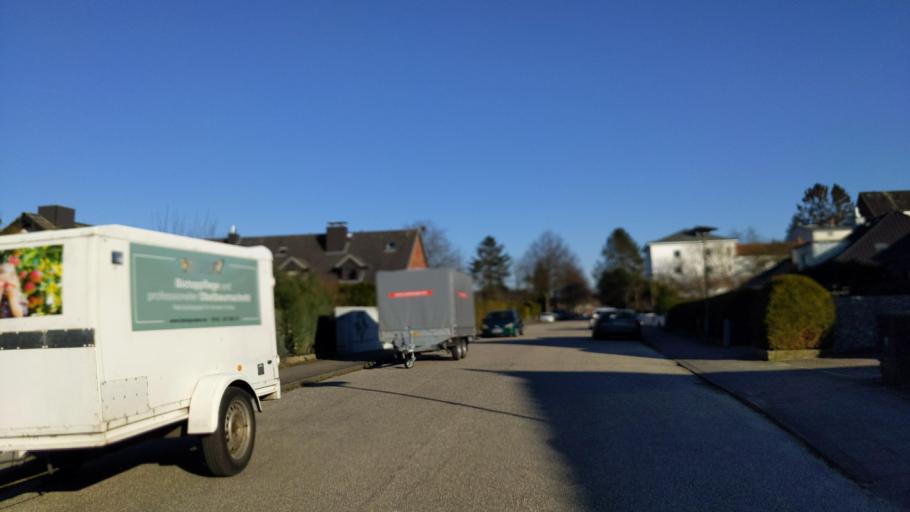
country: DE
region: Schleswig-Holstein
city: Luebeck
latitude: 53.8758
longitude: 10.7121
